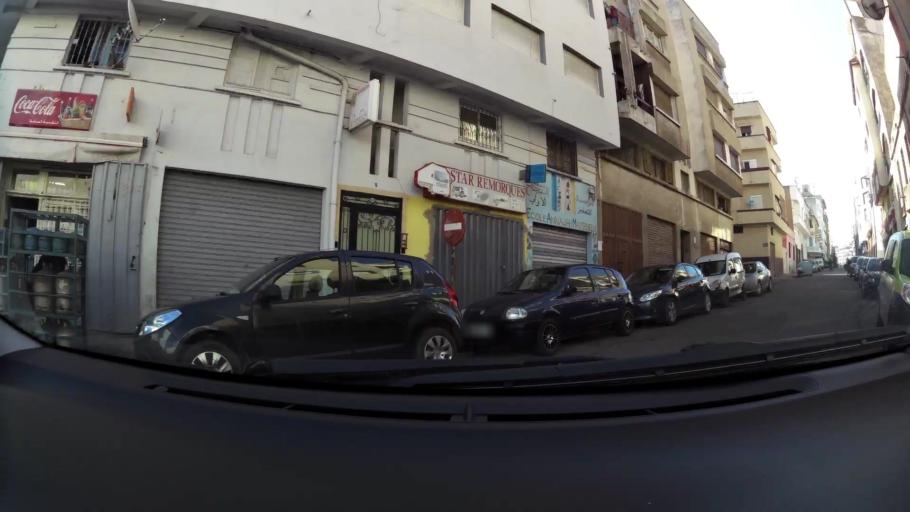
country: MA
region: Grand Casablanca
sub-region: Casablanca
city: Casablanca
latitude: 33.5998
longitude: -7.5875
